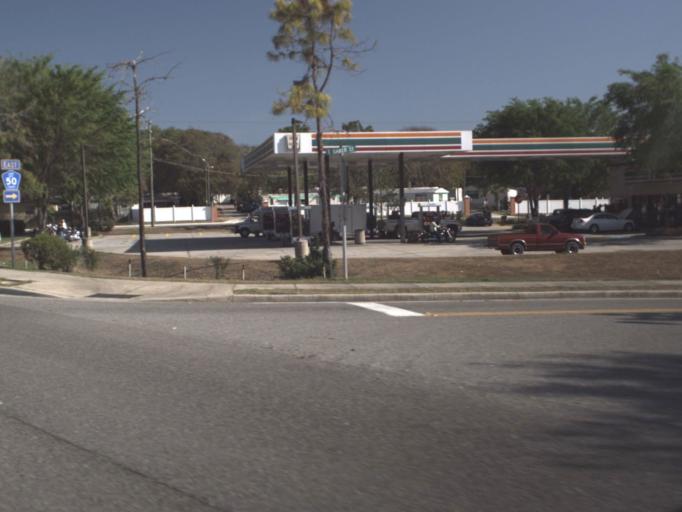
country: US
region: Florida
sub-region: Lake County
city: Minneola
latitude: 28.5746
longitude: -81.7475
